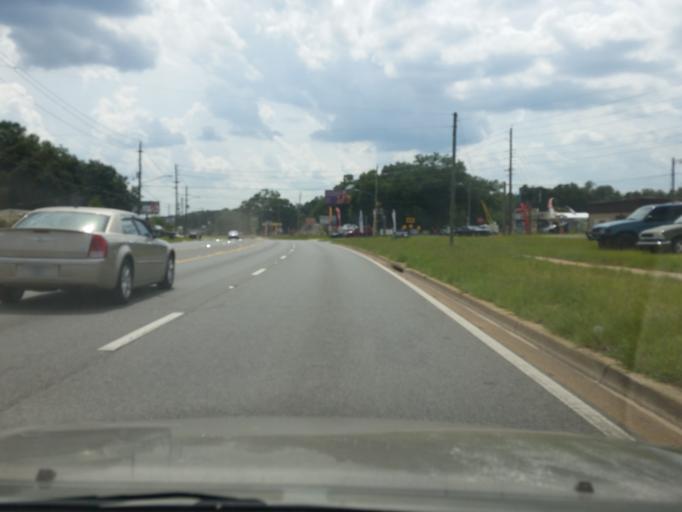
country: US
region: Florida
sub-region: Escambia County
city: Brent
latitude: 30.4642
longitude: -87.2589
